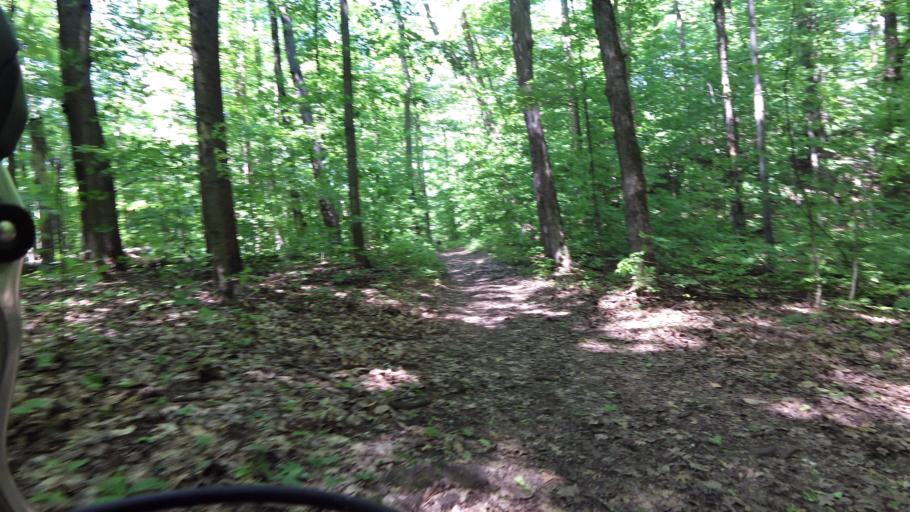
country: CA
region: Quebec
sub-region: Outaouais
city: Wakefield
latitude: 45.5397
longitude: -75.8837
